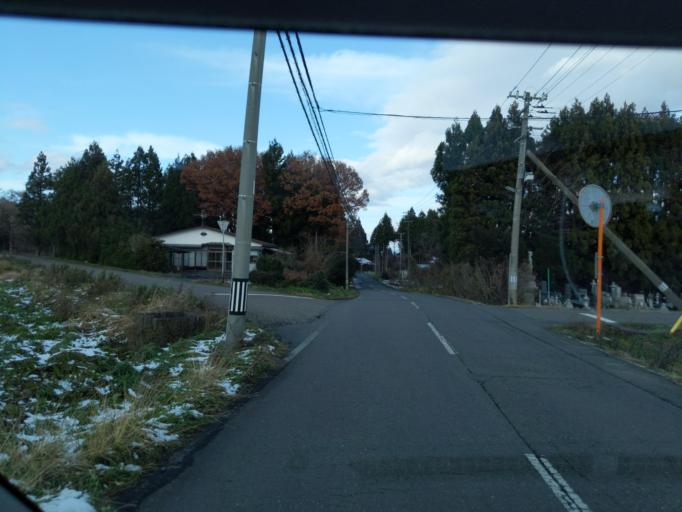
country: JP
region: Iwate
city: Kitakami
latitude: 39.2091
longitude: 141.0493
